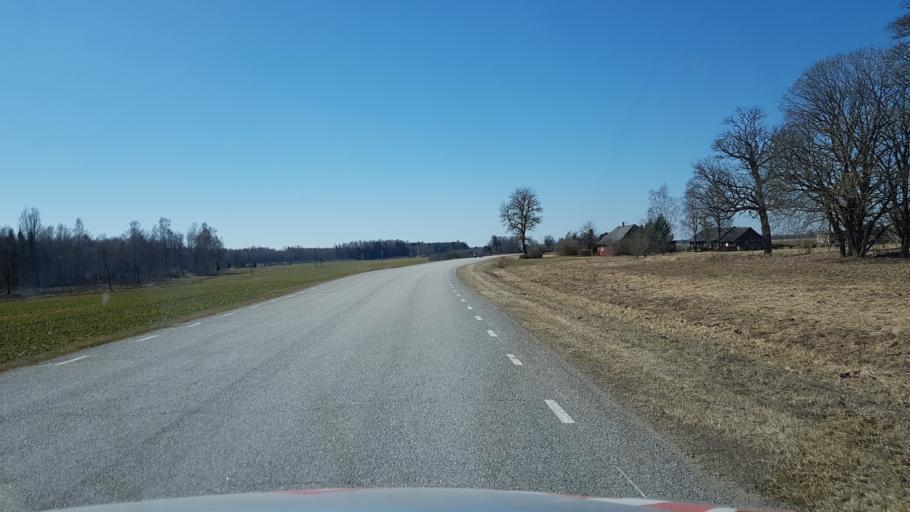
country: EE
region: Laeaene-Virumaa
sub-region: Rakke vald
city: Rakke
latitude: 59.0588
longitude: 26.4656
